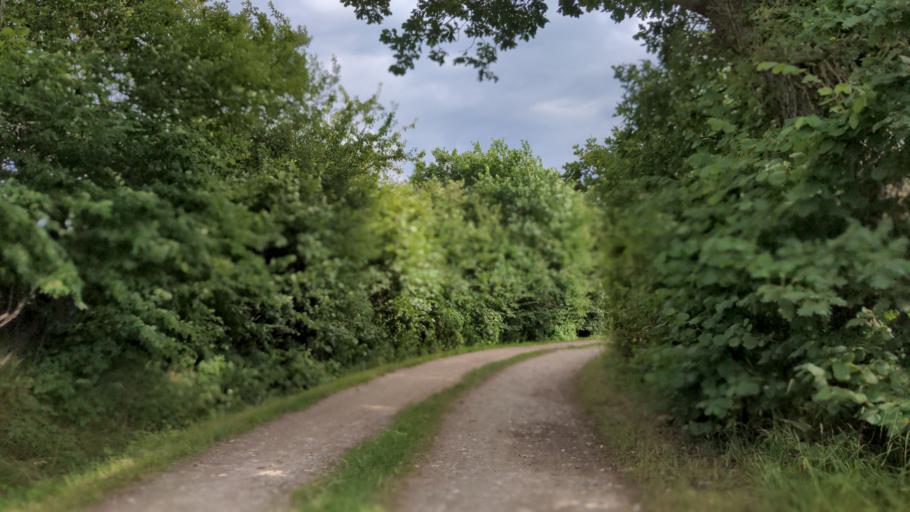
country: DE
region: Schleswig-Holstein
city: Dahme
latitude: 54.2015
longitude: 11.0851
